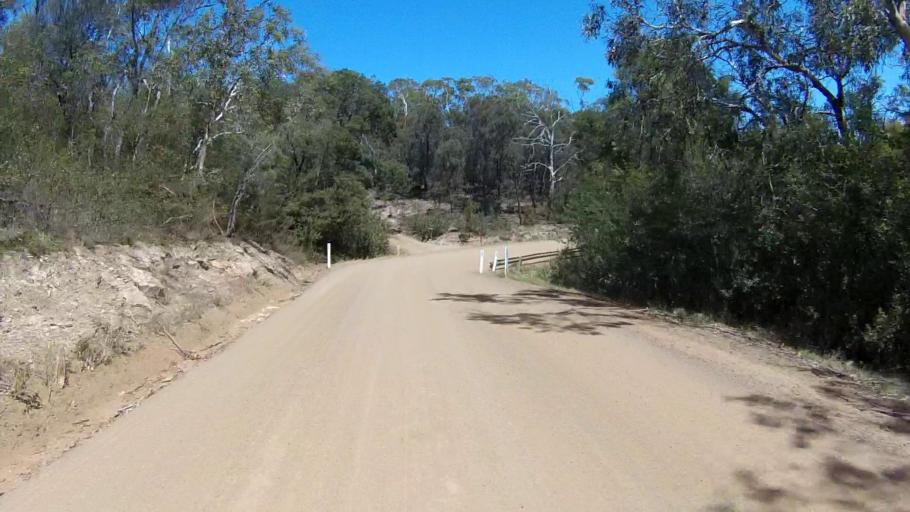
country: AU
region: Tasmania
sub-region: Clarence
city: Lauderdale
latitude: -42.9348
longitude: 147.4632
